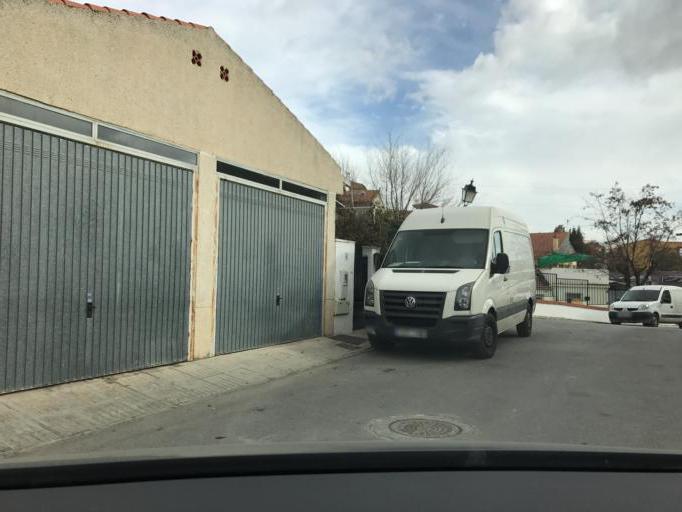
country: ES
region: Andalusia
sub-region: Provincia de Granada
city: Cullar-Vega
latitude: 37.1491
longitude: -3.6783
